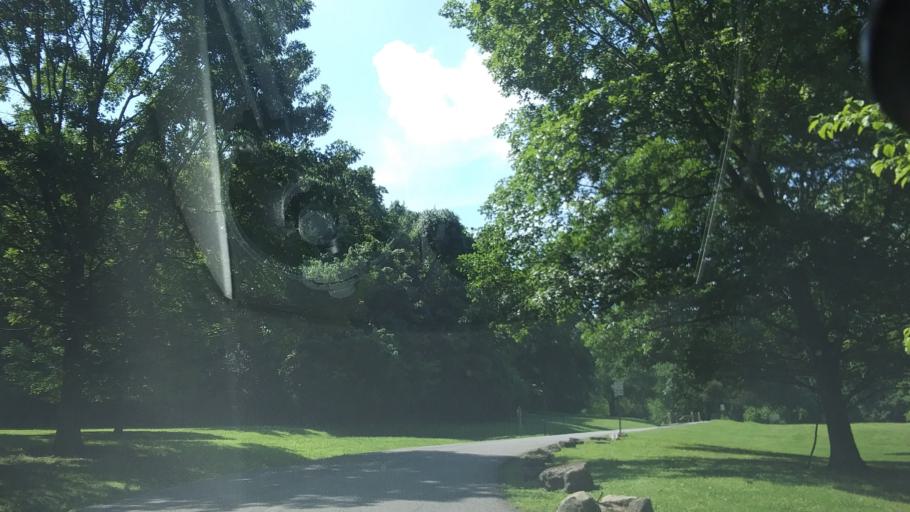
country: US
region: Tennessee
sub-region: Davidson County
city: Belle Meade
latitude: 36.0776
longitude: -86.8861
